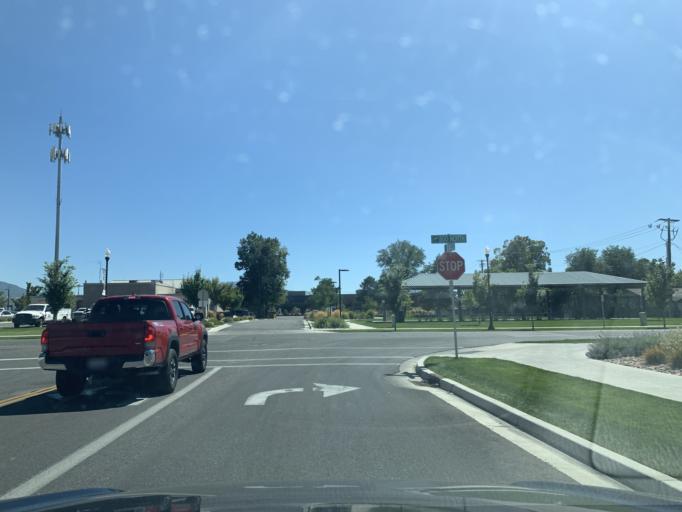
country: US
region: Utah
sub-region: Utah County
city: Provo
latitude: 40.2446
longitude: -111.6641
